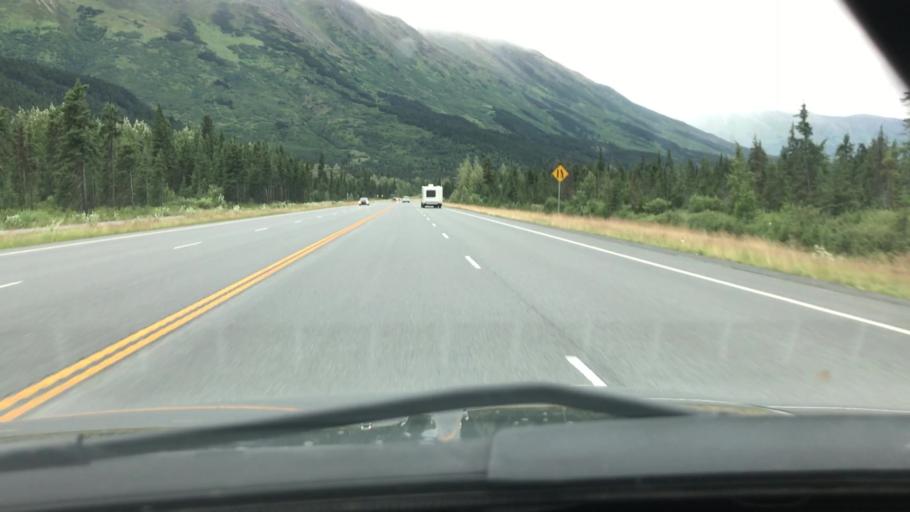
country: US
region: Alaska
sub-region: Anchorage Municipality
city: Girdwood
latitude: 60.7294
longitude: -149.3213
